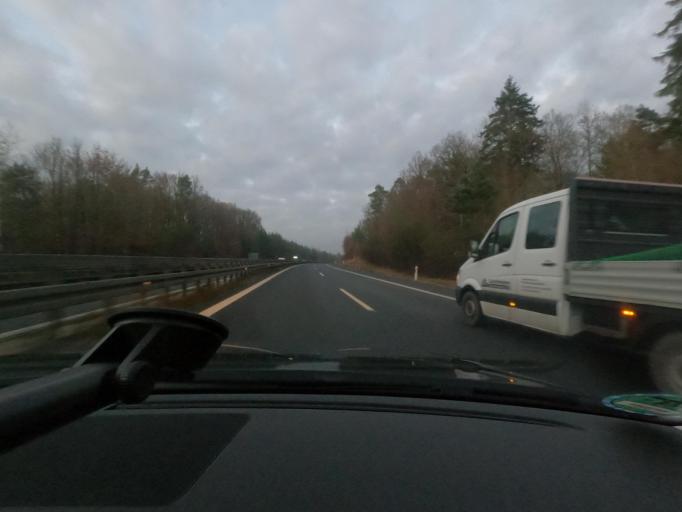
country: DE
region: Bavaria
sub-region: Upper Franconia
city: Zapfendorf
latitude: 50.0265
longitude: 10.9500
